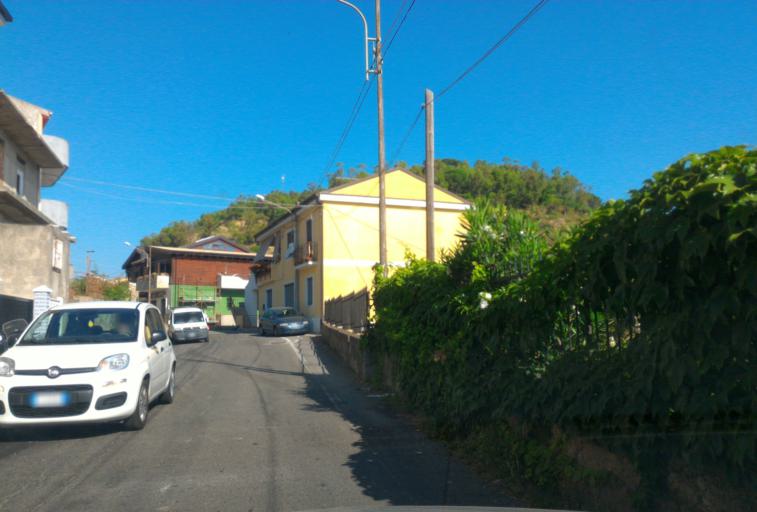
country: IT
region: Calabria
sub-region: Provincia di Crotone
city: Ciro
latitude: 39.3820
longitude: 17.0635
